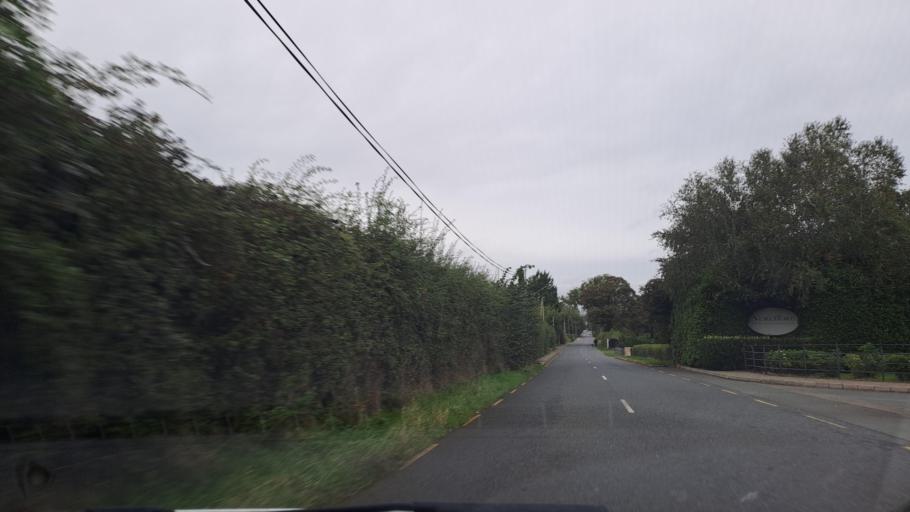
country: IE
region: Ulster
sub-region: County Monaghan
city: Carrickmacross
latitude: 53.9607
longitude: -6.7038
